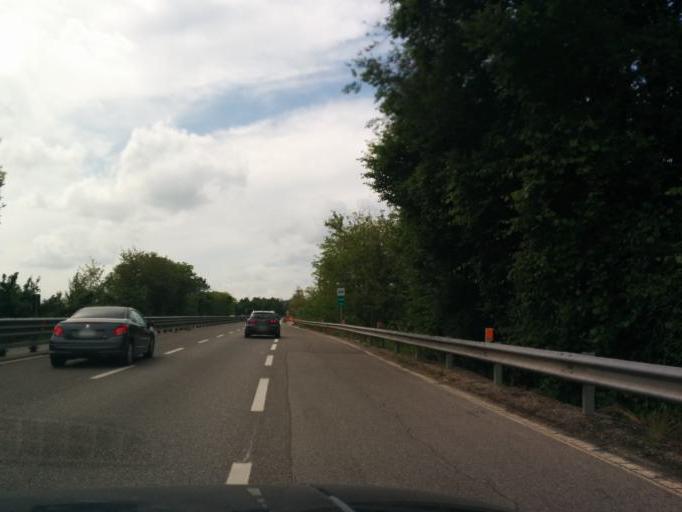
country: IT
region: Tuscany
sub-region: Province of Florence
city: Sambuca
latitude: 43.5902
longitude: 11.2001
